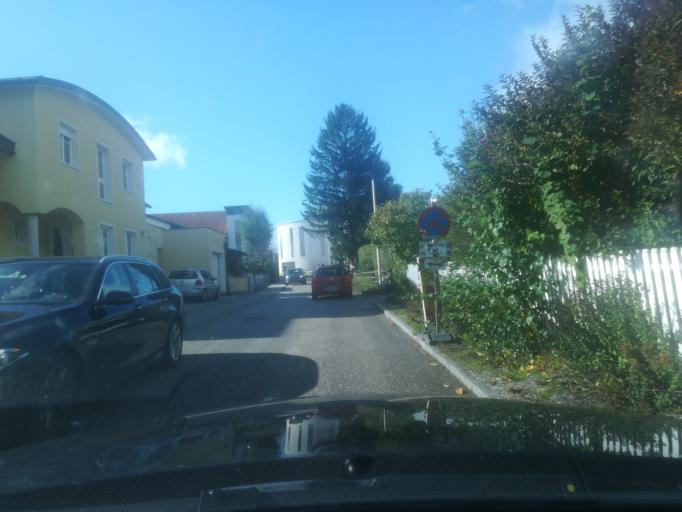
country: AT
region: Upper Austria
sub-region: Politischer Bezirk Urfahr-Umgebung
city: Eidenberg
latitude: 48.3589
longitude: 14.2592
